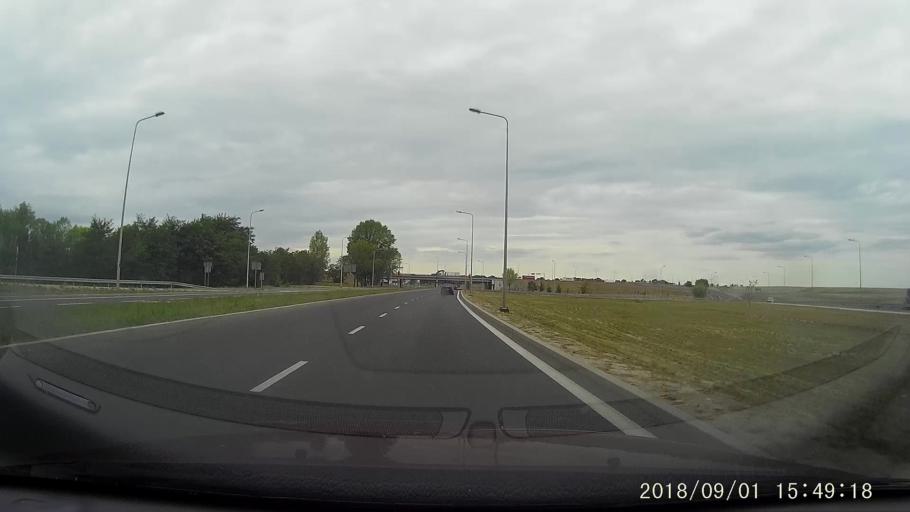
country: PL
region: Lubusz
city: Gorzow Wielkopolski
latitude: 52.7439
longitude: 15.1651
